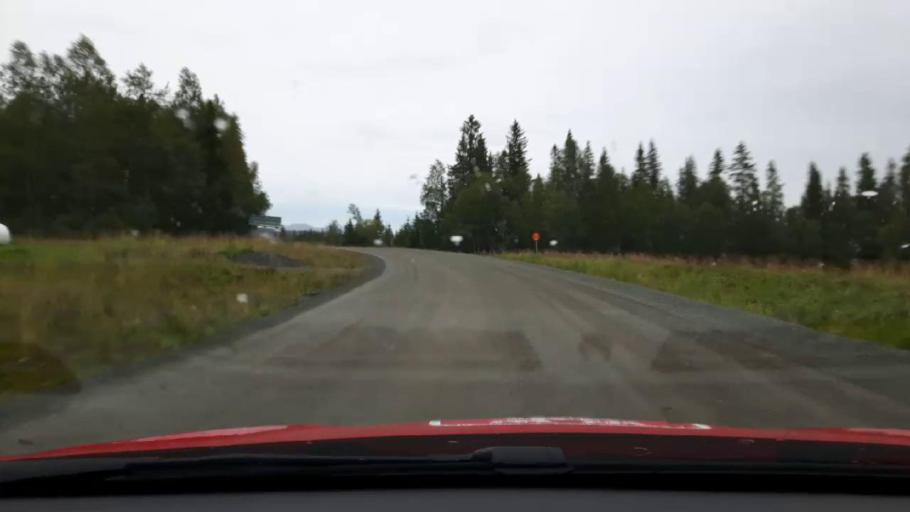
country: SE
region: Jaemtland
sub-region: Are Kommun
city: Are
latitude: 63.4699
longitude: 12.5784
